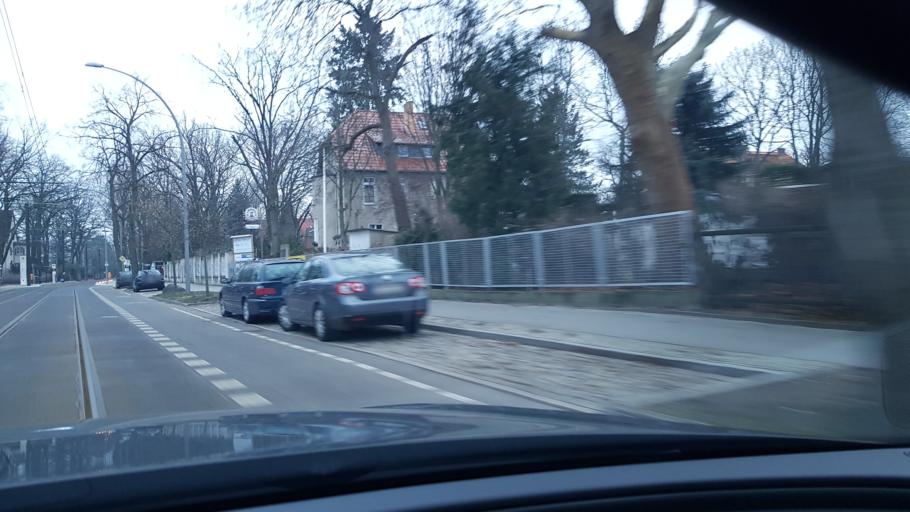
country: DE
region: Berlin
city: Grunau
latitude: 52.4229
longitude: 13.5874
